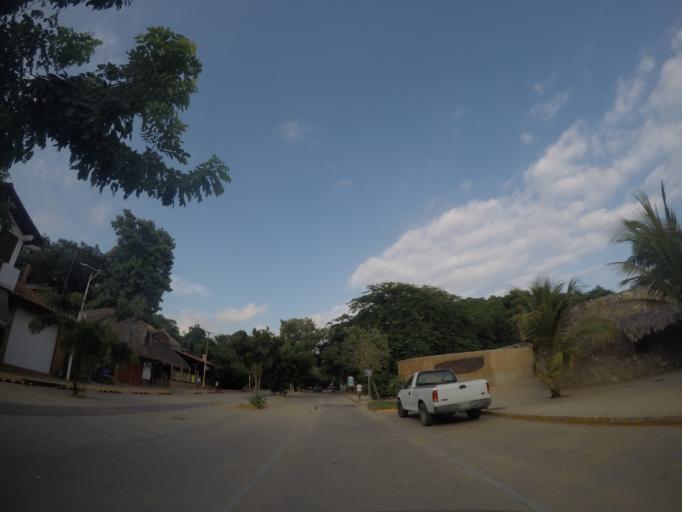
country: MX
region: Oaxaca
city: Santa Maria Tonameca
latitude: 15.6667
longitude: -96.5520
